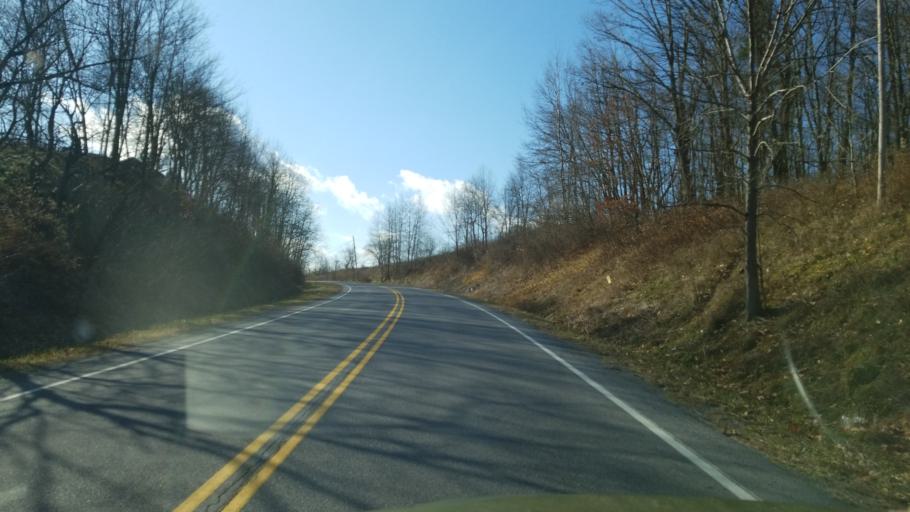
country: US
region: Pennsylvania
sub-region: Clearfield County
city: Hyde
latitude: 40.9985
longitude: -78.4412
